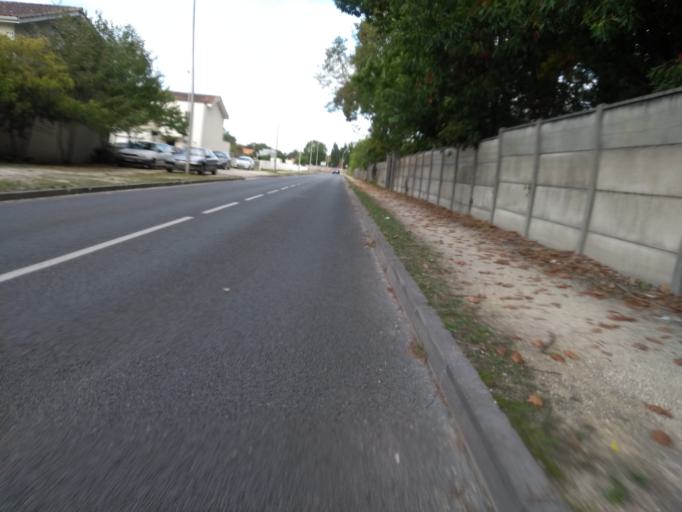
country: FR
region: Aquitaine
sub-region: Departement de la Gironde
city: Cestas
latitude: 44.7842
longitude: -0.6799
